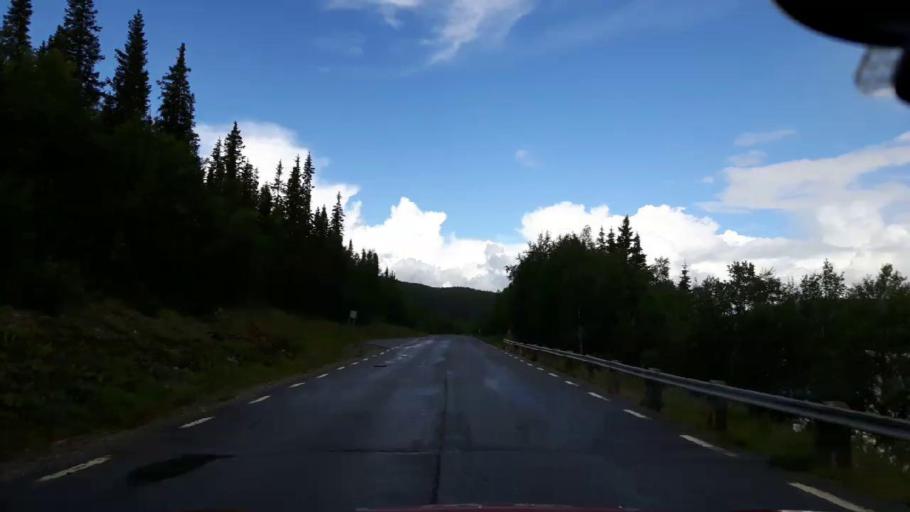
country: SE
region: Vaesterbotten
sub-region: Vilhelmina Kommun
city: Sjoberg
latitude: 65.0083
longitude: 15.1831
